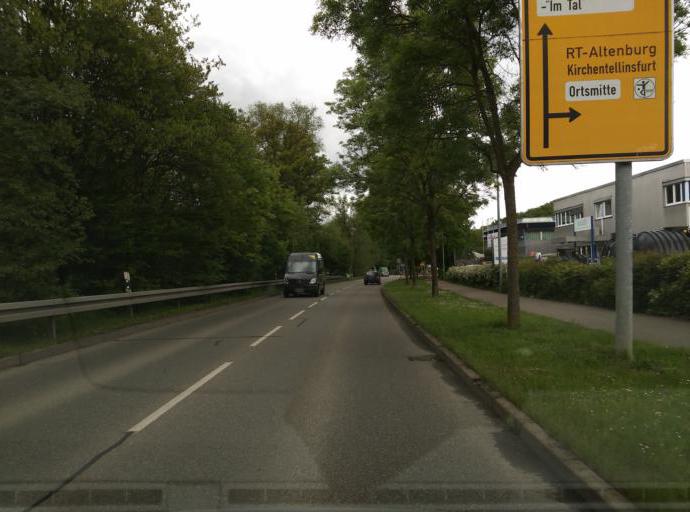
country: DE
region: Baden-Wuerttemberg
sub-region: Tuebingen Region
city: Wannweil
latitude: 48.5226
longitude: 9.1450
